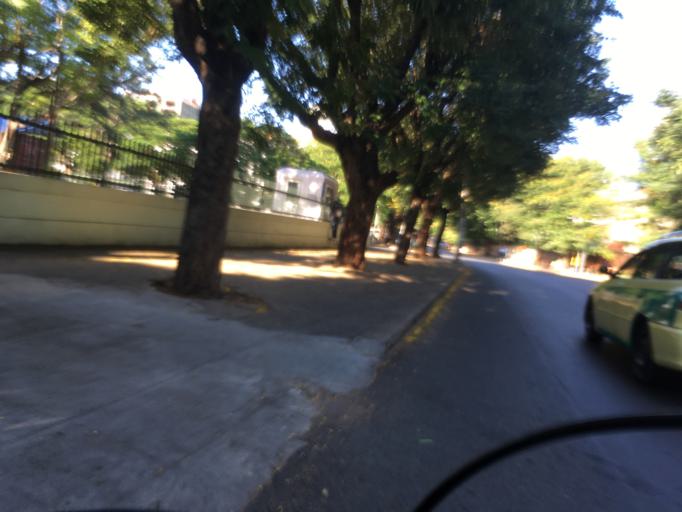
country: MZ
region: Maputo City
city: Maputo
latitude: -25.9695
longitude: 32.5925
